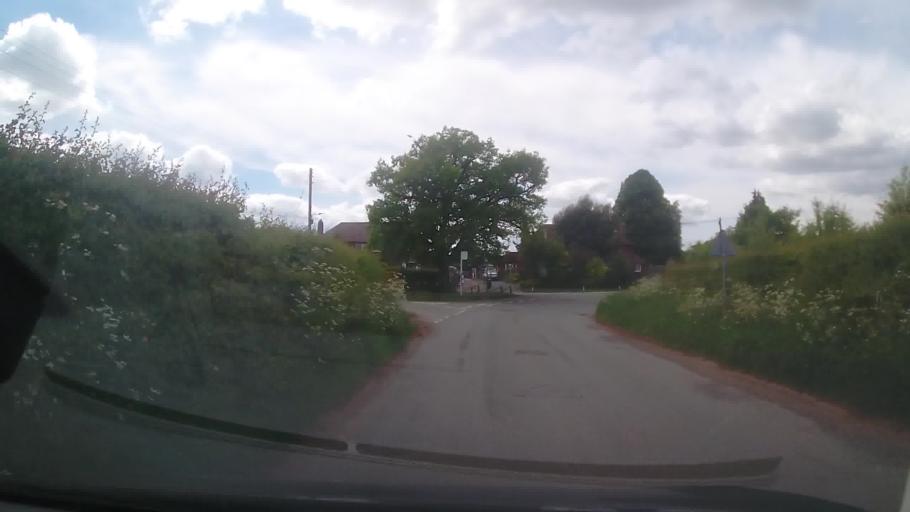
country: GB
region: England
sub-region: Shropshire
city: Clive
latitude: 52.8094
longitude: -2.7379
